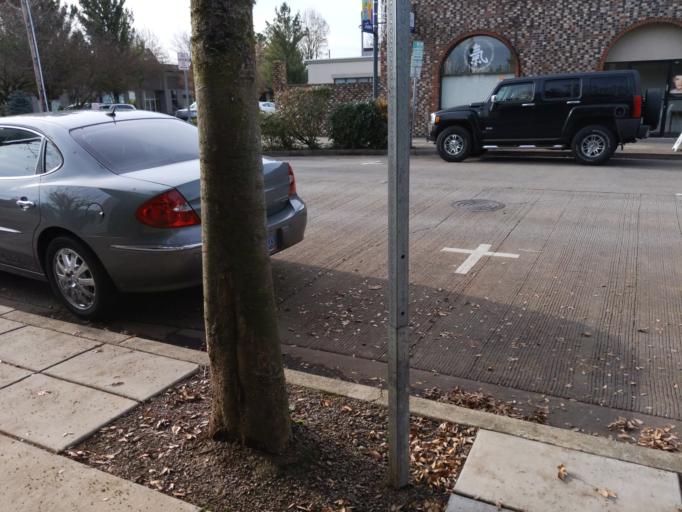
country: US
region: Oregon
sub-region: Washington County
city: Hillsboro
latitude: 45.5218
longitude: -122.9861
